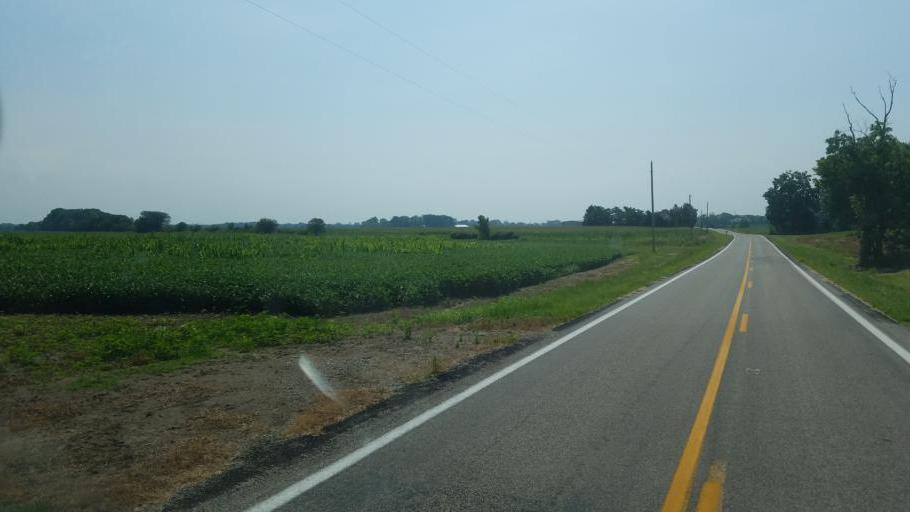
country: US
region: Ohio
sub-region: Union County
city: Richwood
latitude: 40.5546
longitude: -83.3759
